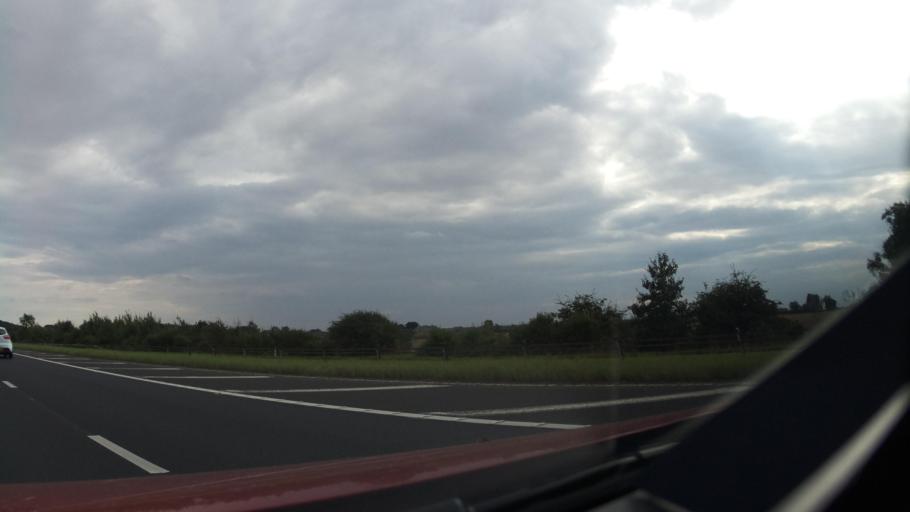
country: GB
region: England
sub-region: County Durham
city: Coxhoe
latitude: 54.7491
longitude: -1.5198
